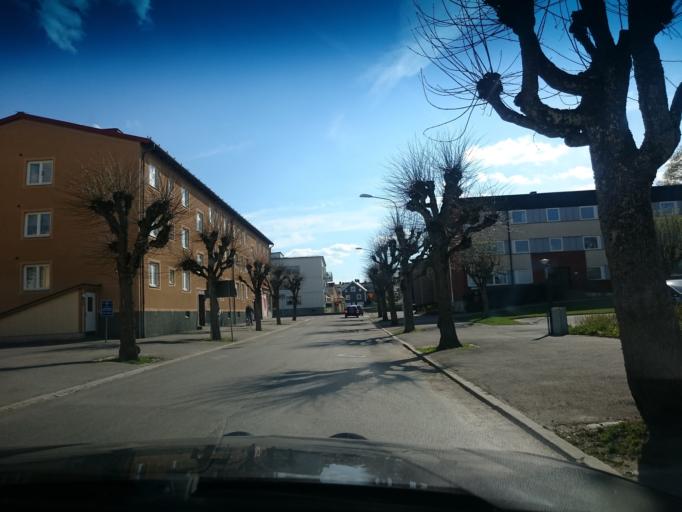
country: SE
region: Joenkoeping
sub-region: Vetlanda Kommun
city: Vetlanda
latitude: 57.4294
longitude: 15.0783
